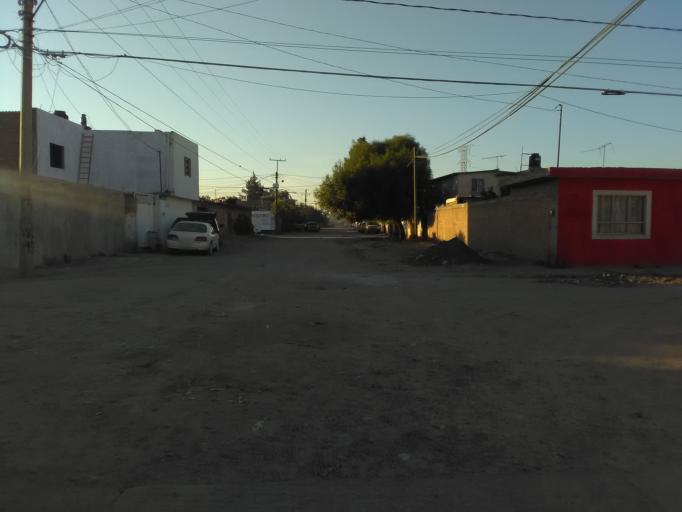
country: MX
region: Durango
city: Victoria de Durango
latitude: 24.0556
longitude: -104.6400
